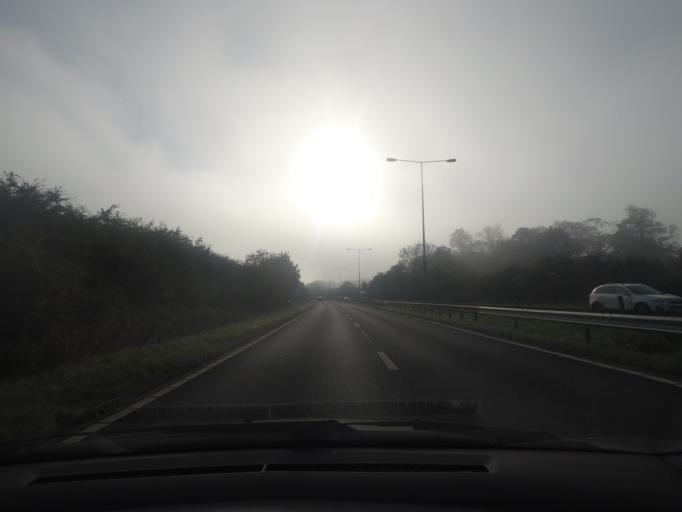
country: GB
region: England
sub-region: East Riding of Yorkshire
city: Welton
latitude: 53.7348
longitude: -0.5588
